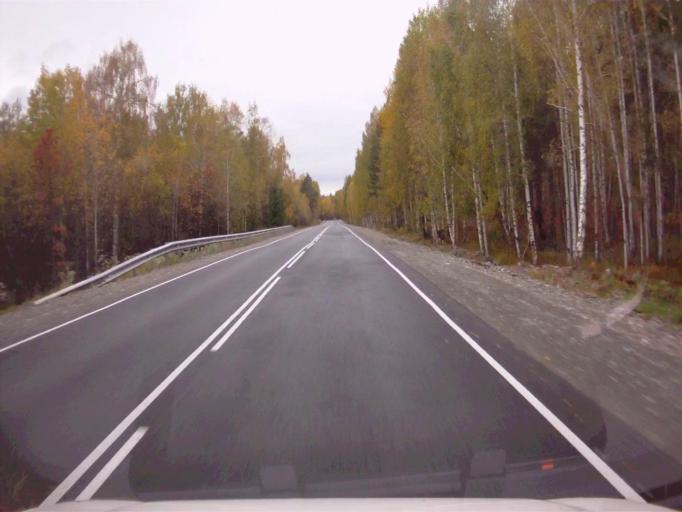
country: RU
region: Chelyabinsk
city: Nyazepetrovsk
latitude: 56.0629
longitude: 59.7074
